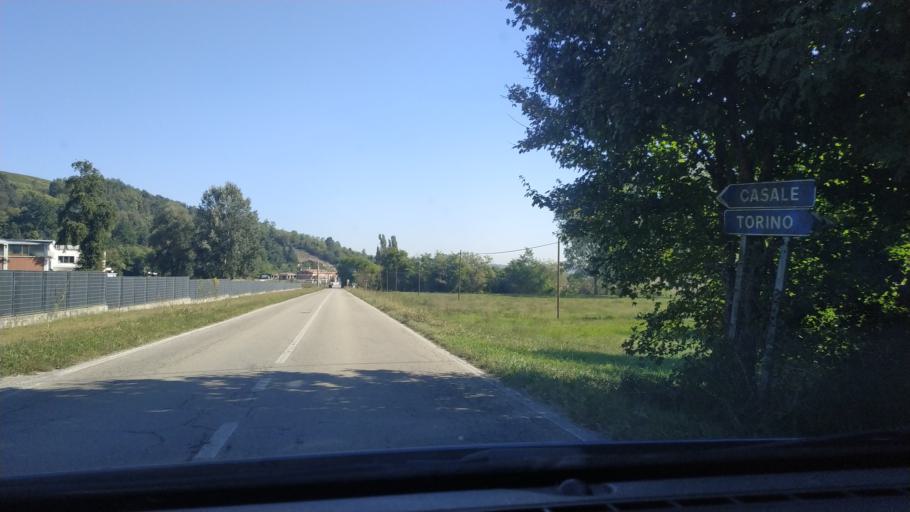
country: IT
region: Piedmont
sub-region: Provincia di Alessandria
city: Cerrina
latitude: 45.1067
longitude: 8.2012
